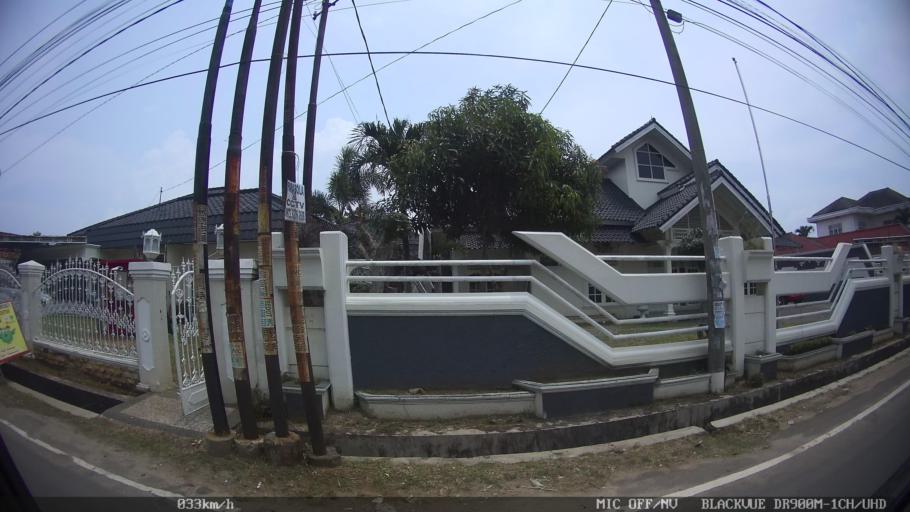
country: ID
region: Lampung
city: Bandarlampung
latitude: -5.4169
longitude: 105.2736
